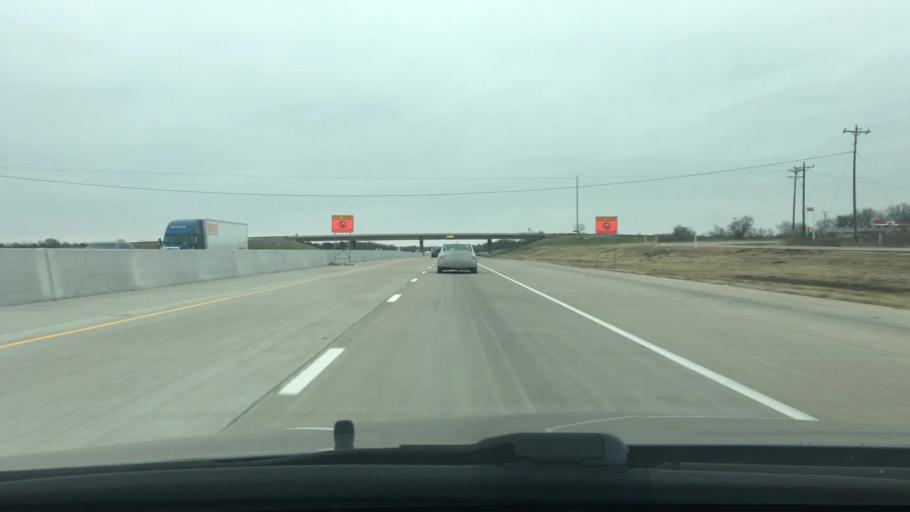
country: US
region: Texas
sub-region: Freestone County
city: Wortham
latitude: 31.8807
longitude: -96.3464
